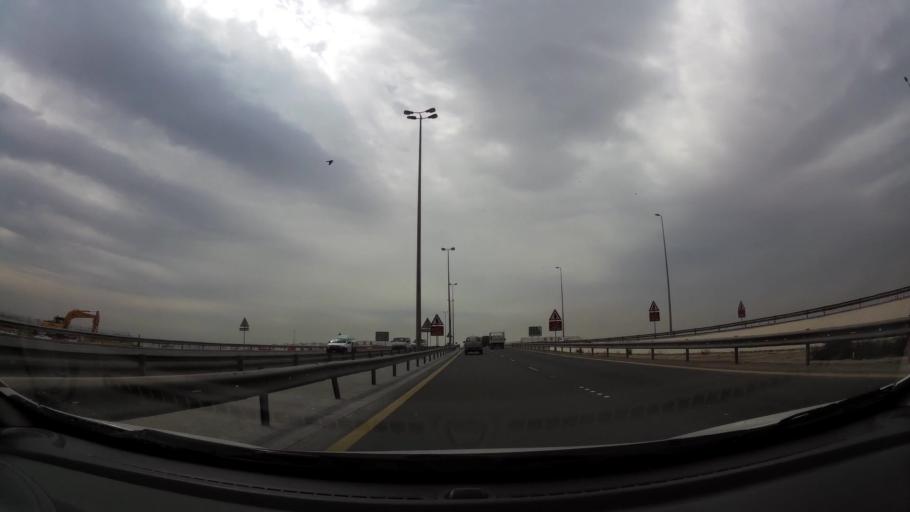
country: BH
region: Manama
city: Manama
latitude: 26.1961
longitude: 50.5899
